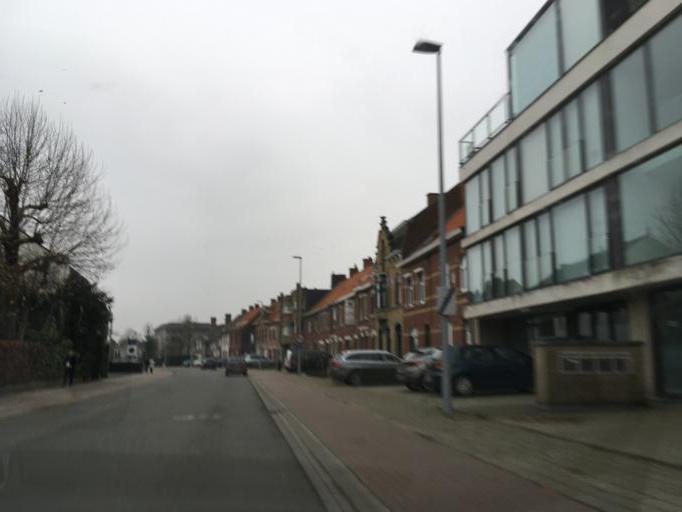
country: BE
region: Flanders
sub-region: Provincie West-Vlaanderen
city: Roeselare
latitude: 50.9324
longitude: 3.1571
